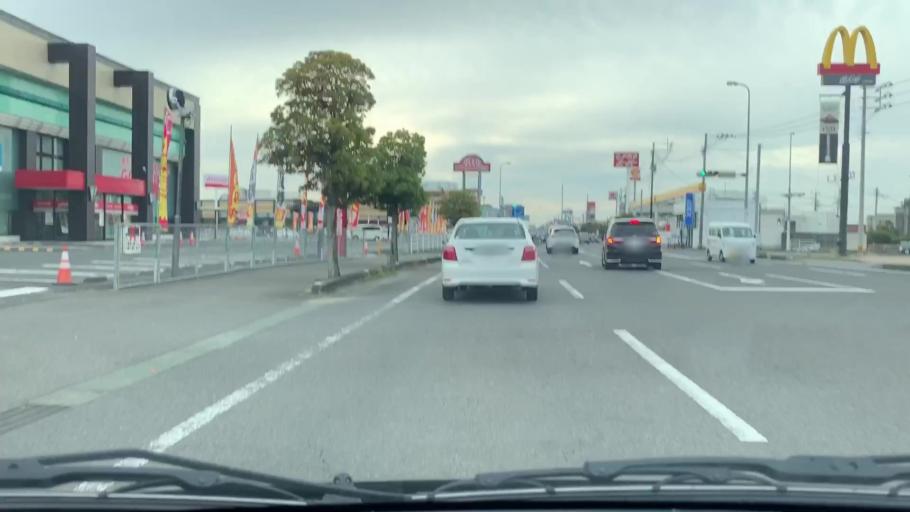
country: JP
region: Saga Prefecture
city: Saga-shi
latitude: 33.2935
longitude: 130.2848
